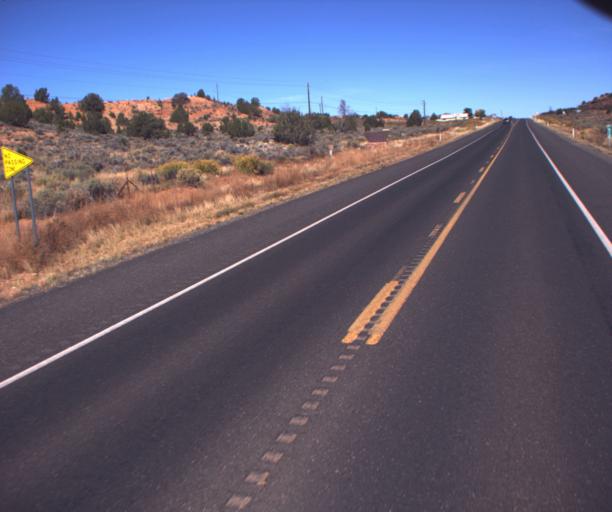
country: US
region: Arizona
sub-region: Coconino County
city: Fredonia
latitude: 36.9847
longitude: -112.5298
